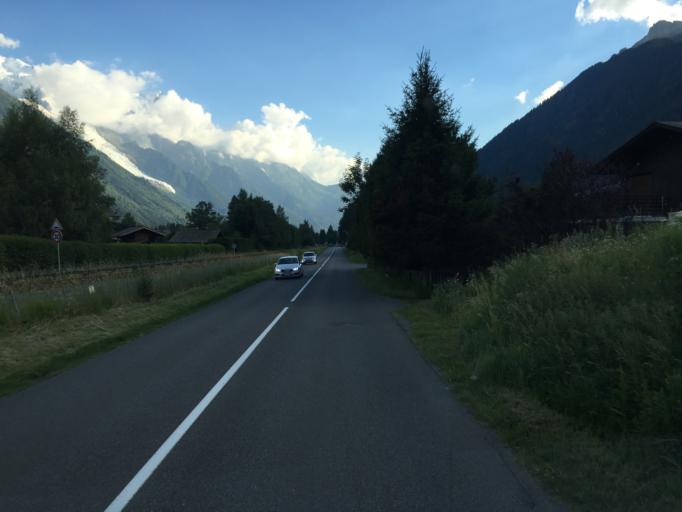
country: FR
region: Rhone-Alpes
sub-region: Departement de la Haute-Savoie
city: Chamonix-Mont-Blanc
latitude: 45.9478
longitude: 6.8960
